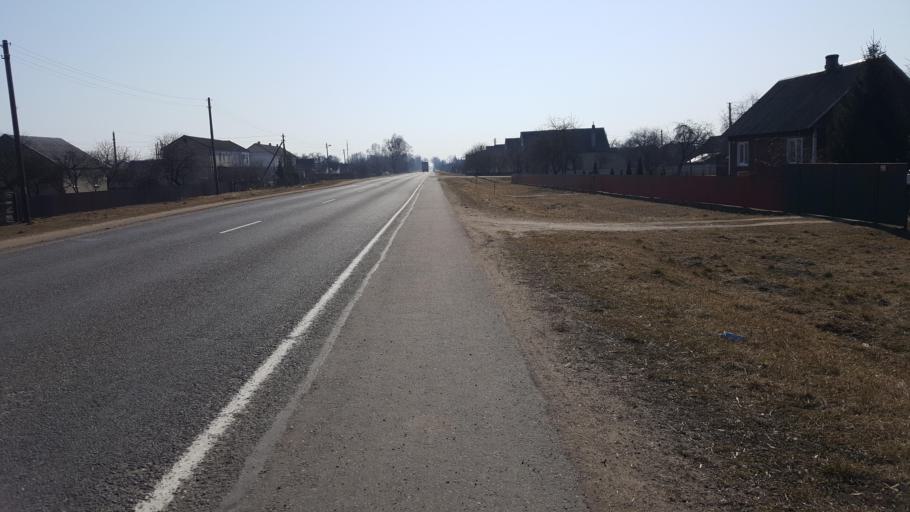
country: BY
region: Brest
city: Kamyanyets
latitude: 52.3238
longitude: 23.9176
